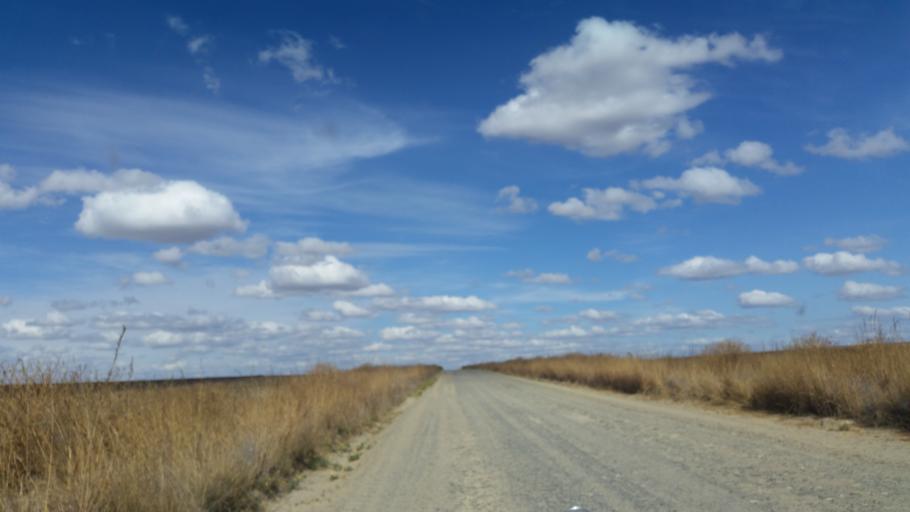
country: ZA
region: Orange Free State
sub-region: Thabo Mofutsanyana District Municipality
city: Bethlehem
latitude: -28.1525
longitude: 28.6577
